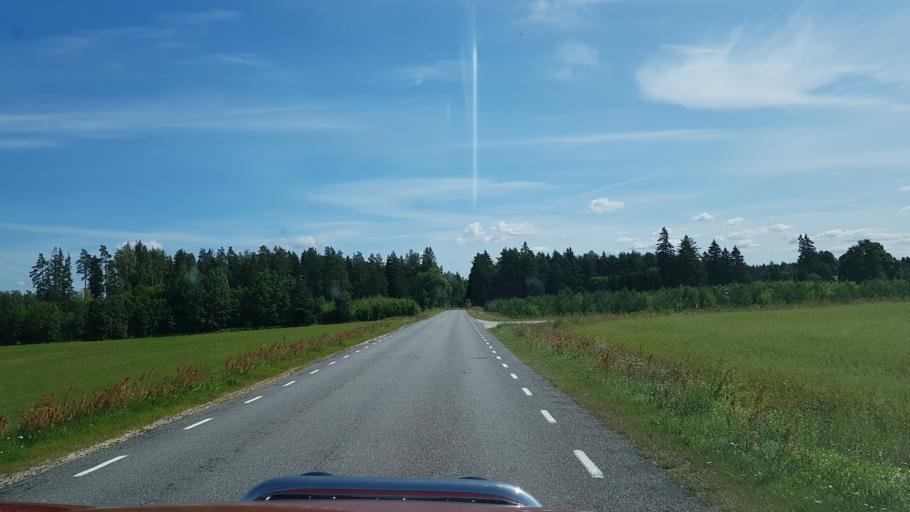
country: EE
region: Laeaene-Virumaa
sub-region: Tapa vald
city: Tapa
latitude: 59.1805
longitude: 25.9714
